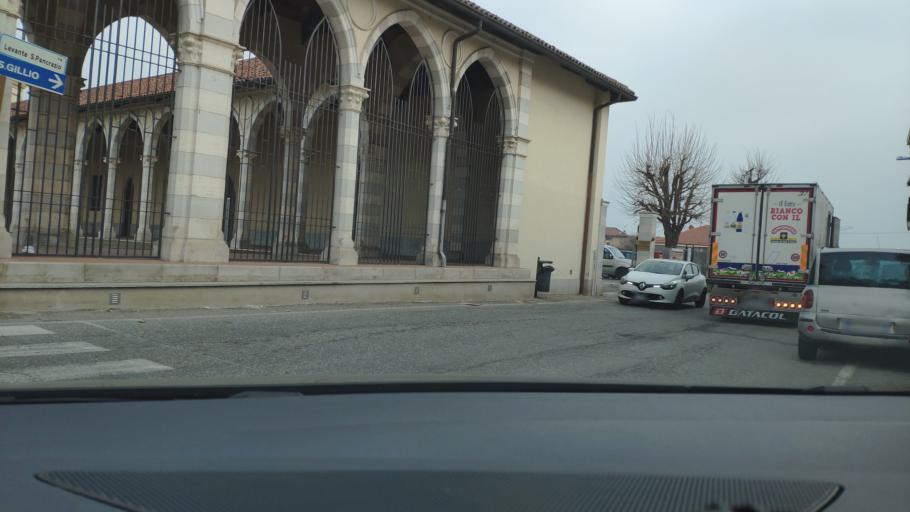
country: IT
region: Piedmont
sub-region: Provincia di Torino
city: Pianezza
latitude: 45.1134
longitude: 7.5422
